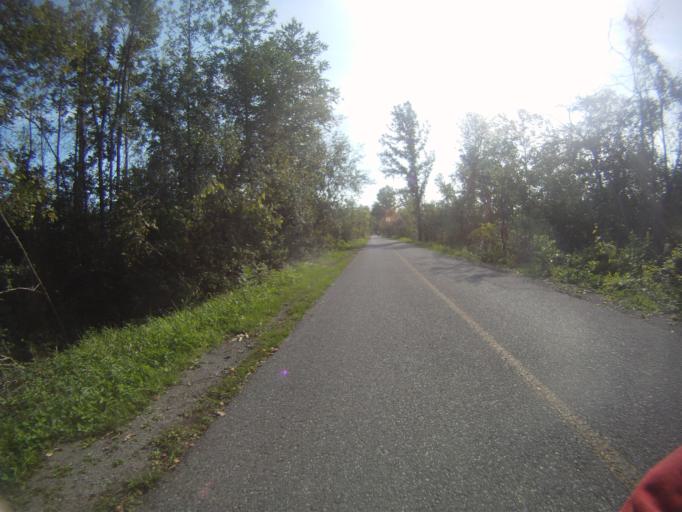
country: CA
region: Ontario
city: Bells Corners
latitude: 45.3414
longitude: -75.8566
